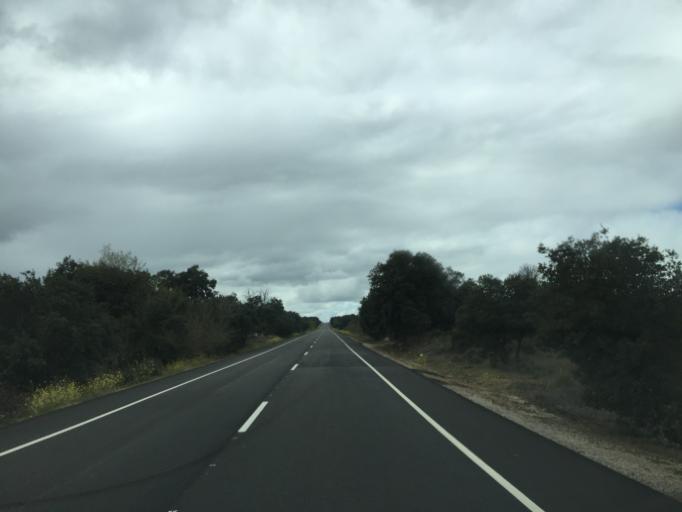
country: ES
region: Castille and Leon
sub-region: Provincia de Zamora
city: Torregamones
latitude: 41.4772
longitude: -6.1932
